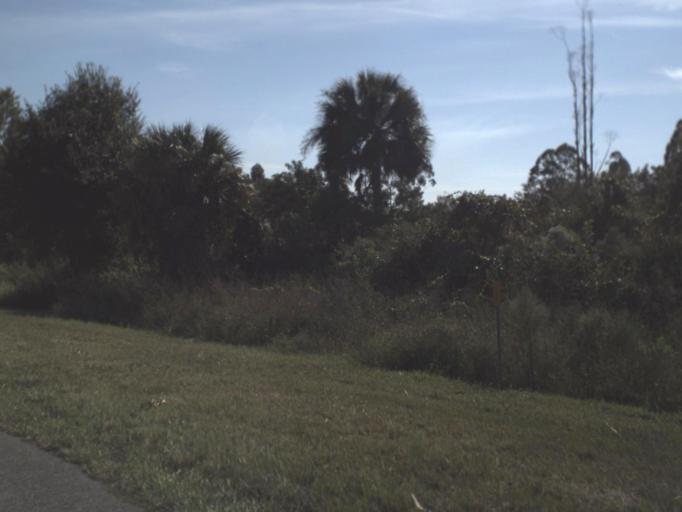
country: US
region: Florida
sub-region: Hendry County
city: Port LaBelle
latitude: 26.9802
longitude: -81.3211
